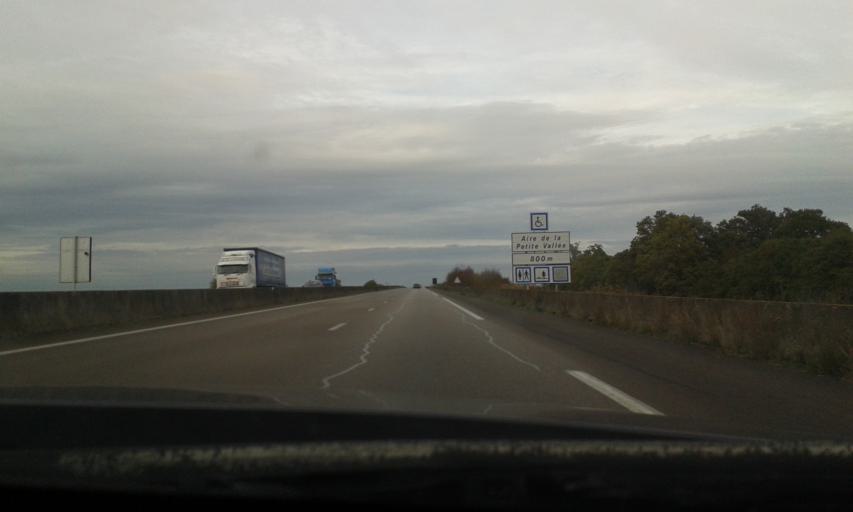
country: FR
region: Haute-Normandie
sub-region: Departement de l'Eure
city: La Madeleine-de-Nonancourt
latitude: 48.8577
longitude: 1.1788
